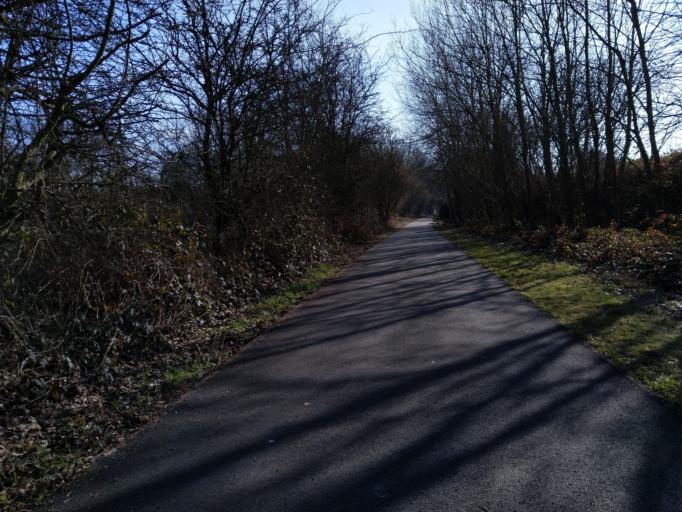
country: BE
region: Wallonia
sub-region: Province du Hainaut
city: Frameries
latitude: 50.4284
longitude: 3.8931
